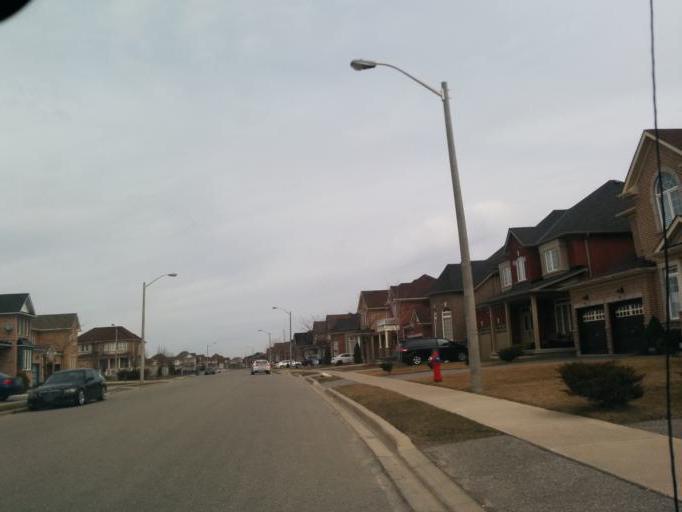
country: CA
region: Ontario
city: Brampton
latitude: 43.7187
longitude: -79.8270
